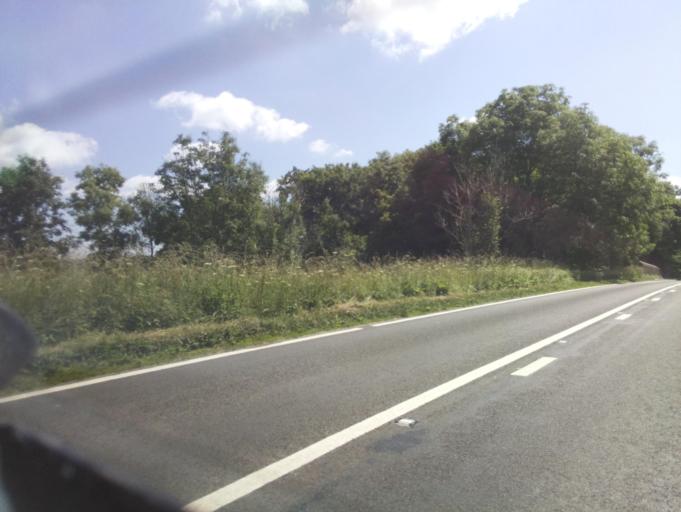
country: GB
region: England
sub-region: Derbyshire
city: Buxton
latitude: 53.2387
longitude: -1.8926
